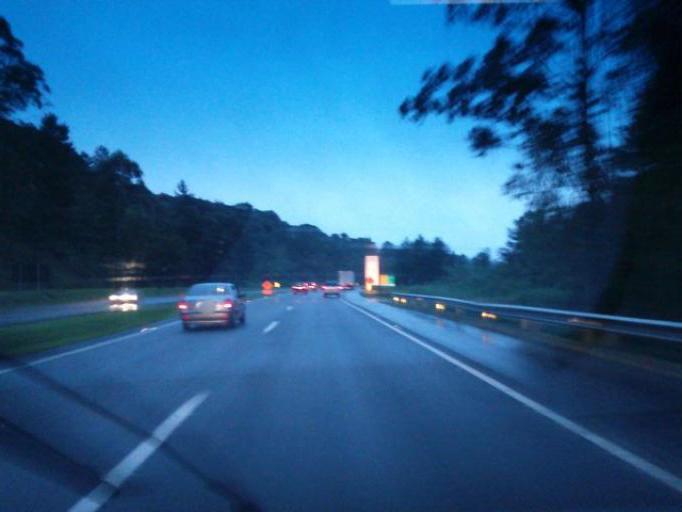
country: BR
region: Sao Paulo
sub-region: Juquitiba
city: Juquitiba
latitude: -23.9393
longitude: -47.0878
